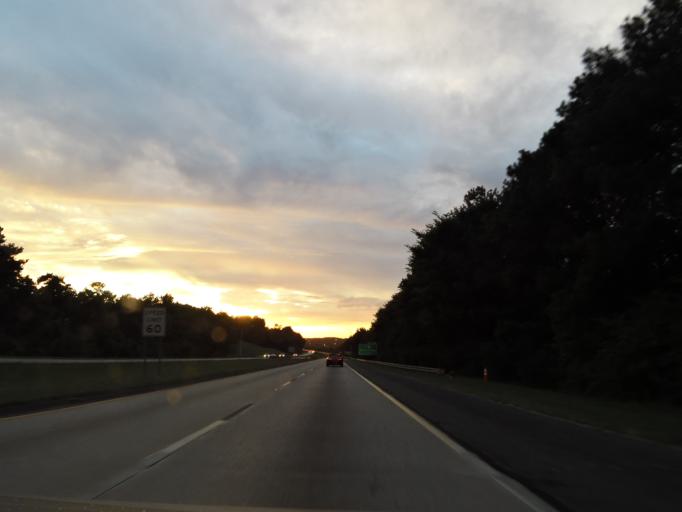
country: US
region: Alabama
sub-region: Jefferson County
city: Irondale
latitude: 33.5861
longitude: -86.6809
